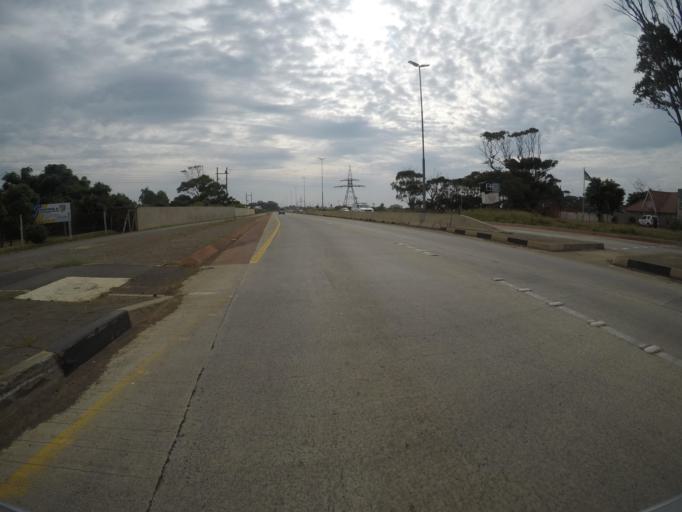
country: ZA
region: Eastern Cape
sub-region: Buffalo City Metropolitan Municipality
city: East London
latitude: -32.9372
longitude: 27.9830
